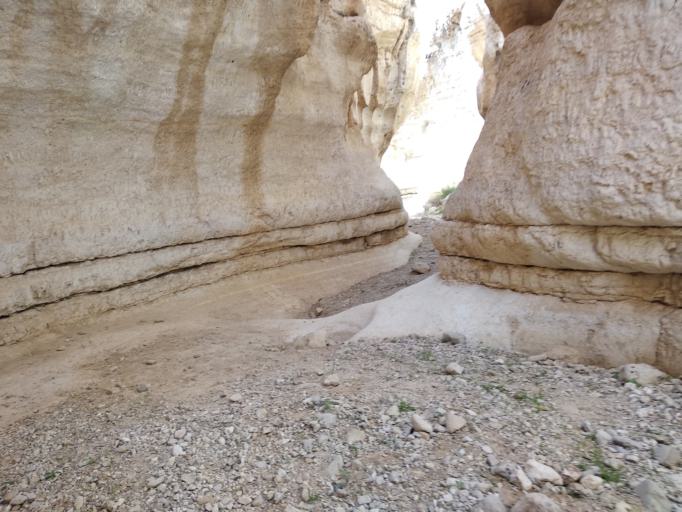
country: JO
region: Karak
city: Safi
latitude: 31.0103
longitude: 35.2891
